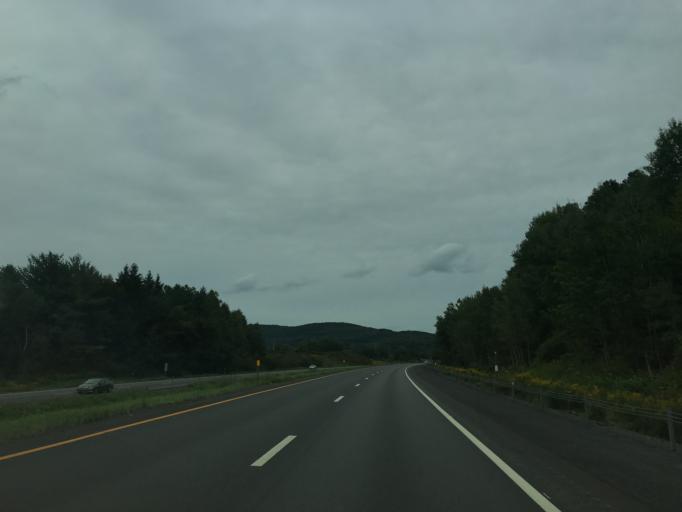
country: US
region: New York
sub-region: Delaware County
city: Sidney
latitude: 42.3116
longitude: -75.3544
